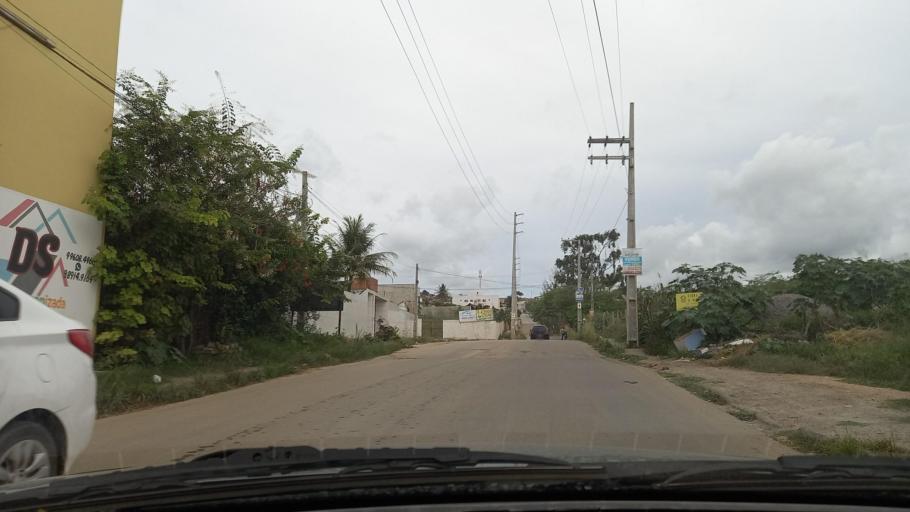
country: BR
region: Pernambuco
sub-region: Gravata
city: Gravata
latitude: -8.2060
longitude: -35.5804
